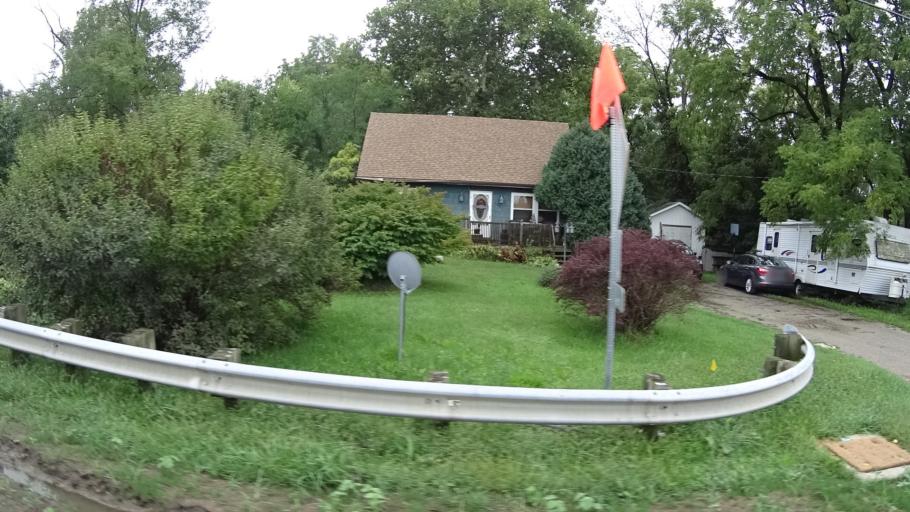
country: US
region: Ohio
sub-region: Erie County
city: Sandusky
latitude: 41.3966
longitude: -82.7088
